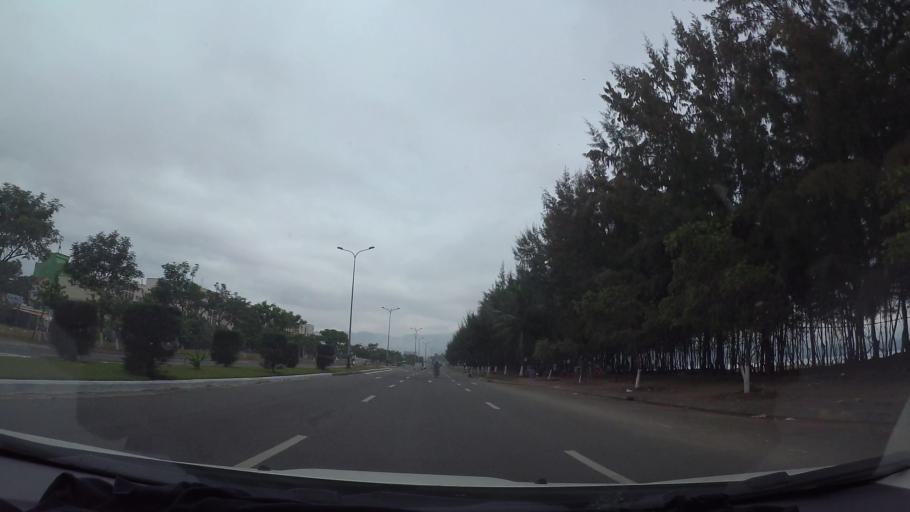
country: VN
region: Da Nang
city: Lien Chieu
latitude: 16.1067
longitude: 108.1353
